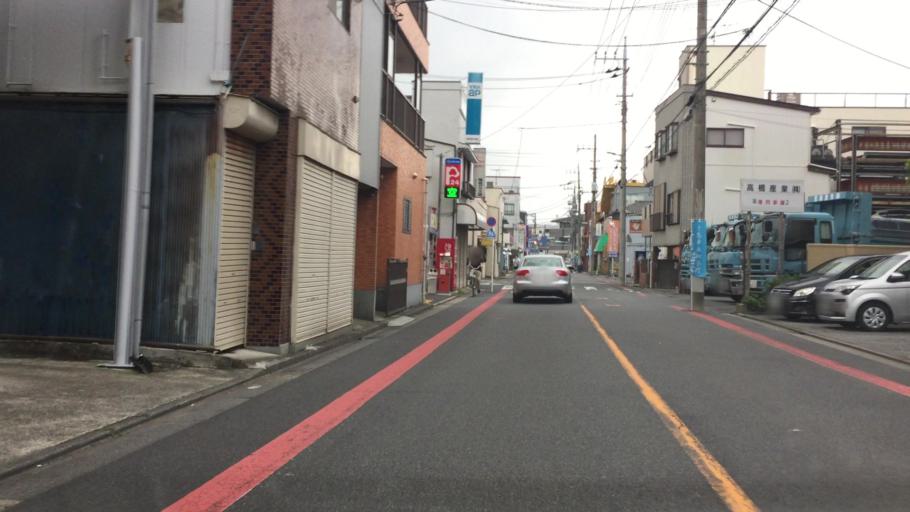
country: JP
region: Chiba
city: Matsudo
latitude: 35.7467
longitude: 139.8428
